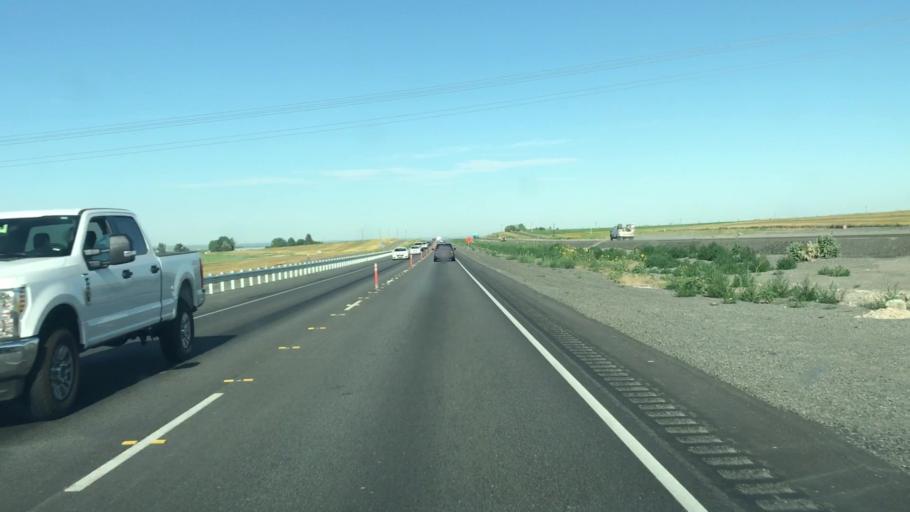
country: US
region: Idaho
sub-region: Twin Falls County
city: Hansen
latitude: 42.5761
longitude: -114.2387
